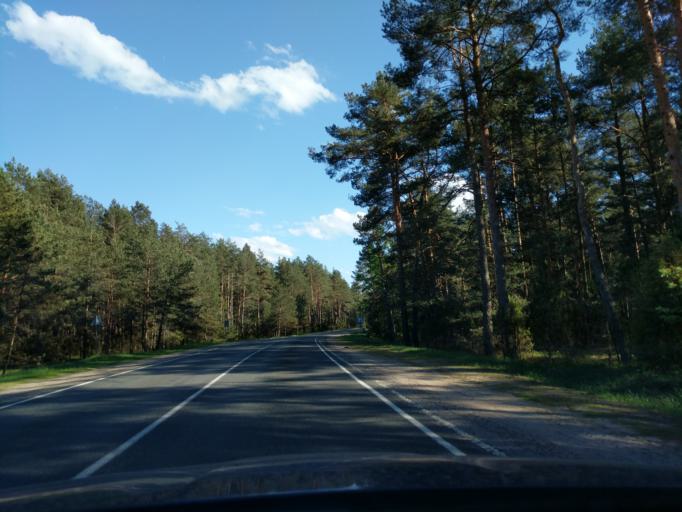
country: BY
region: Minsk
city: Myadzyel
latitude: 54.8325
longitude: 26.9399
